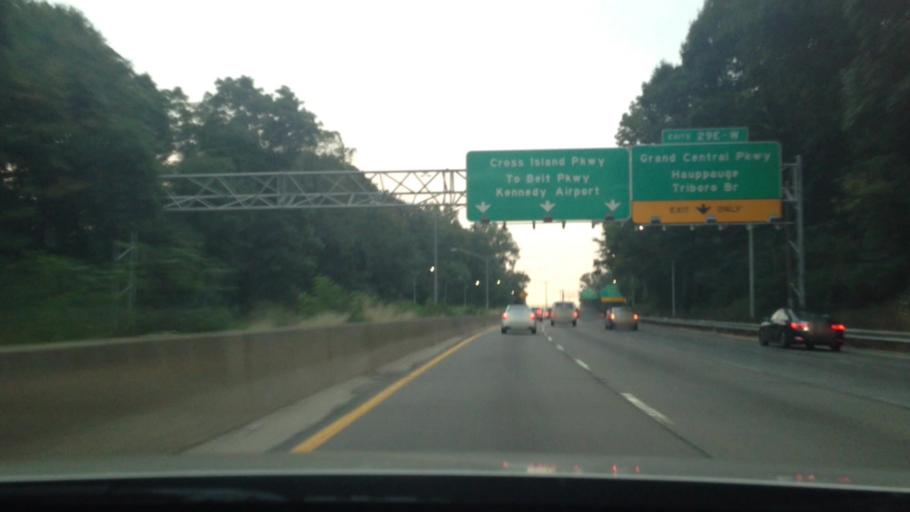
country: US
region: New York
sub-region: Nassau County
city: Bellerose Terrace
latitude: 40.7483
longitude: -73.7382
